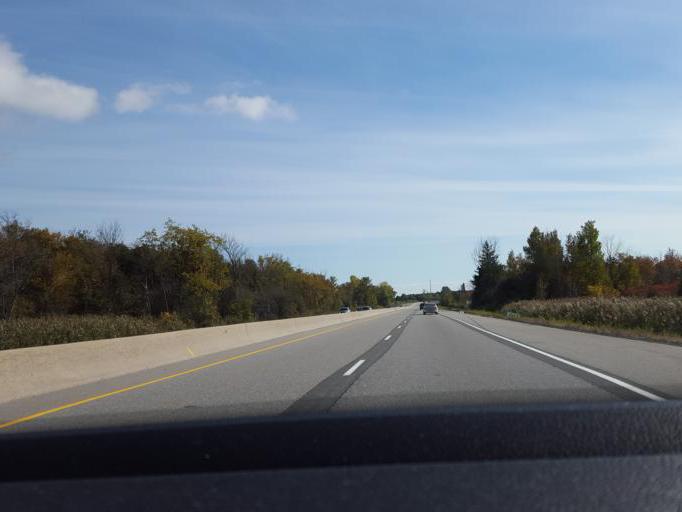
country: CA
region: Ontario
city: Oshawa
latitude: 43.9834
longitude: -78.6144
